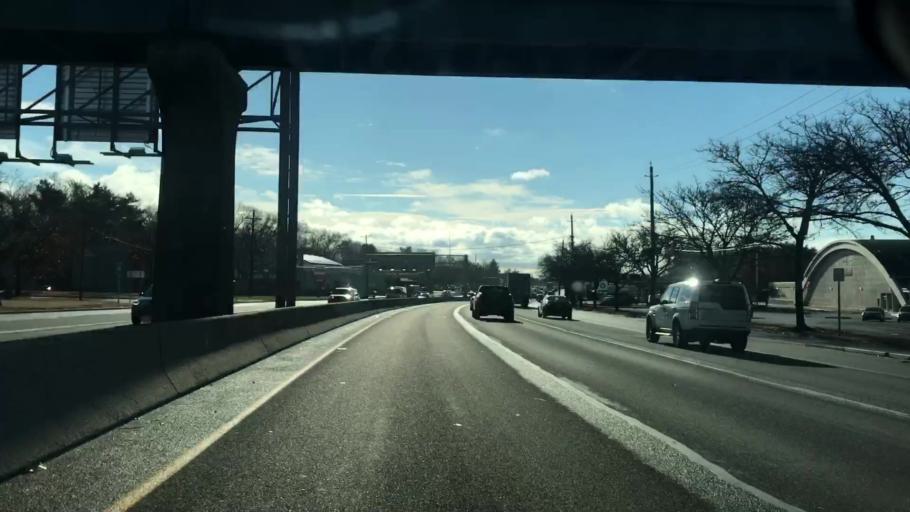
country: US
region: New Jersey
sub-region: Bergen County
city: Ho-Ho-Kus
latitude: 40.9791
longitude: -74.0836
